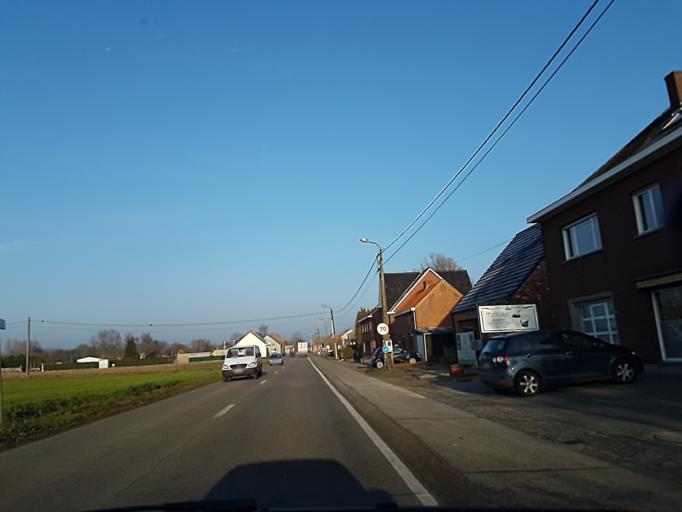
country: BE
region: Flanders
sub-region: Provincie Antwerpen
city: Heist-op-den-Berg
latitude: 51.0566
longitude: 4.7326
